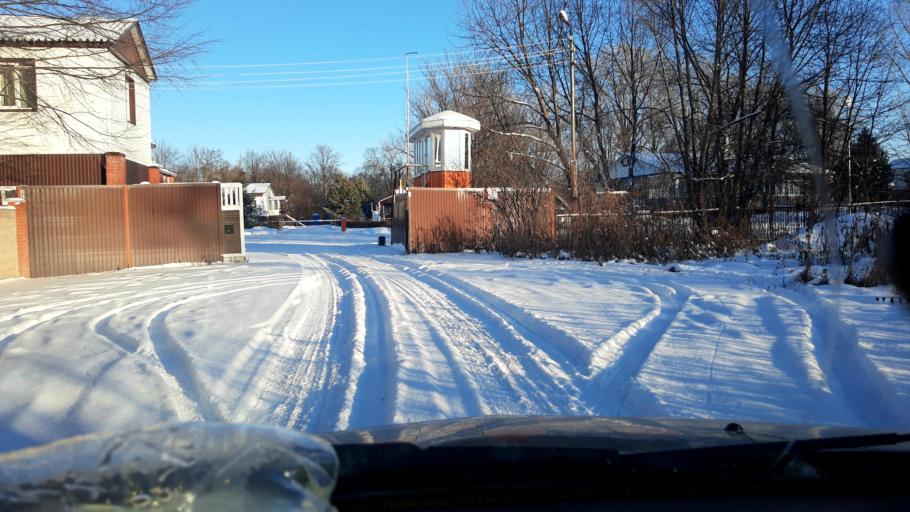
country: RU
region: Bashkortostan
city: Ufa
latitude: 54.6532
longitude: 55.9749
